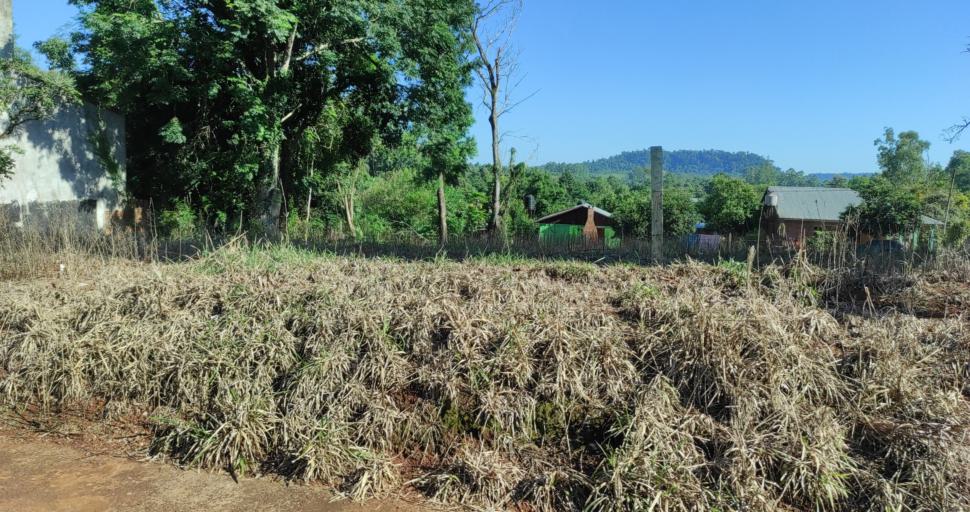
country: AR
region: Misiones
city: El Soberbio
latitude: -27.2941
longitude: -54.1963
